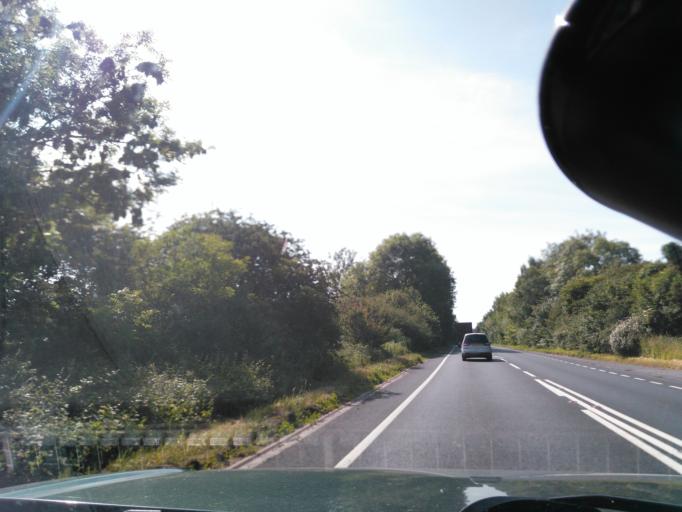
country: GB
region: England
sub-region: Wiltshire
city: Whiteparish
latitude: 51.0020
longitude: -1.6634
